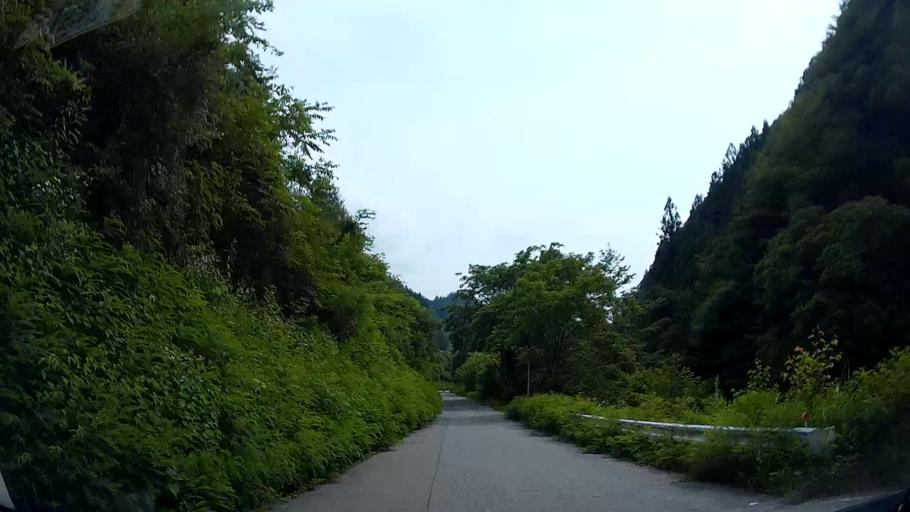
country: JP
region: Nagano
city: Iida
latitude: 35.4499
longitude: 137.9963
